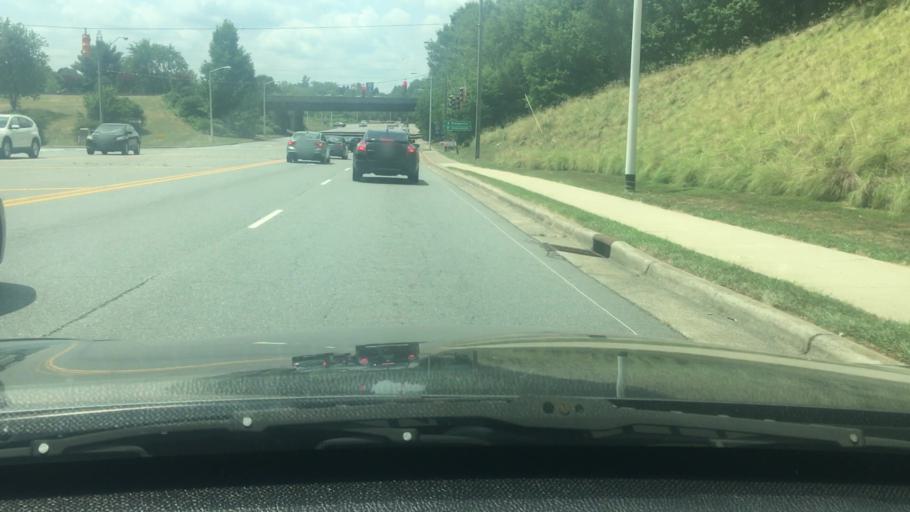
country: US
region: North Carolina
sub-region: Forsyth County
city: Winston-Salem
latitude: 36.0660
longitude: -80.2994
